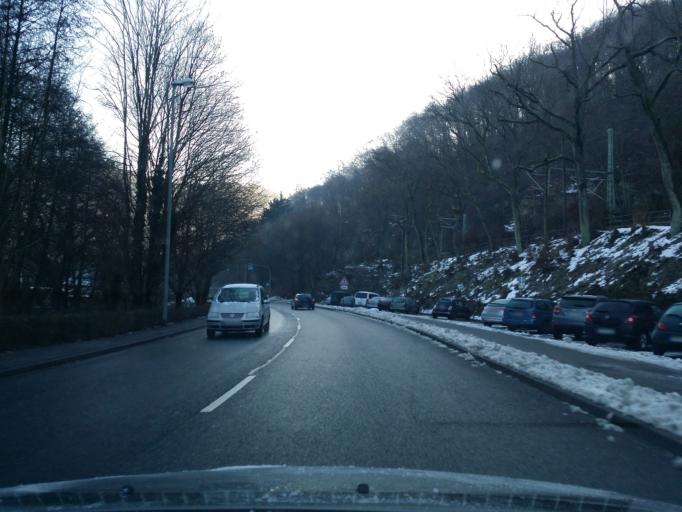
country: DE
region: Hesse
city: Eppstein
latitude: 50.1390
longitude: 8.3900
